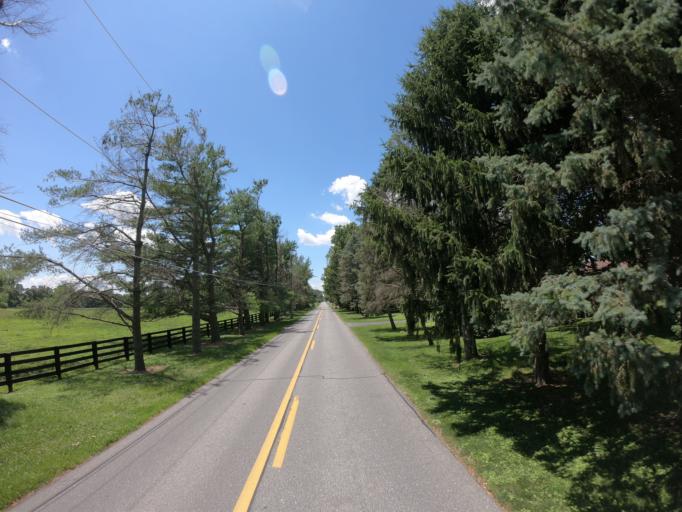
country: US
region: Delaware
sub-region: New Castle County
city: Middletown
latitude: 39.4812
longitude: -75.7503
